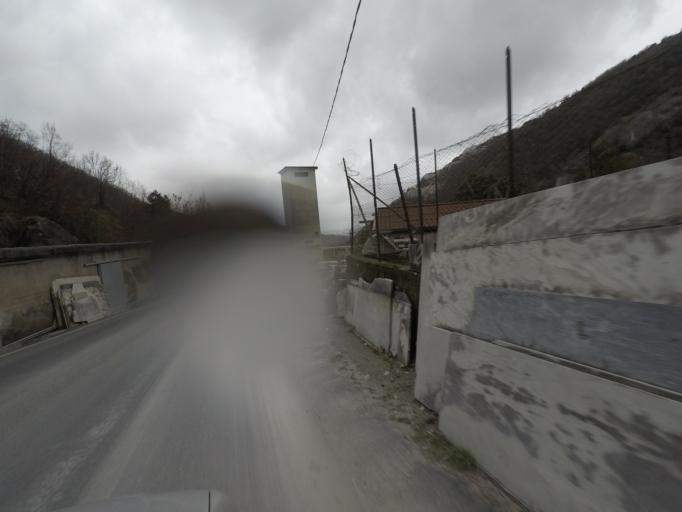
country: IT
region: Tuscany
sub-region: Provincia di Massa-Carrara
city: Montignoso
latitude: 44.0810
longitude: 10.1439
